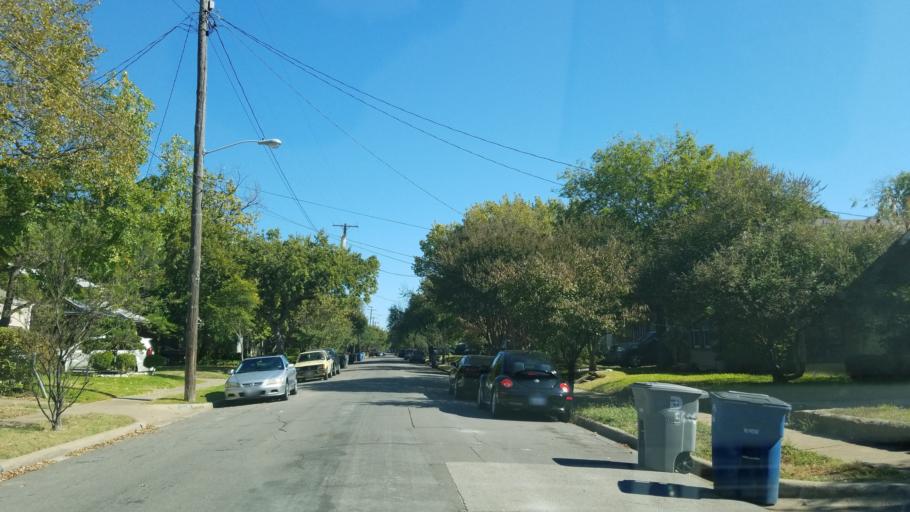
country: US
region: Texas
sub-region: Dallas County
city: Highland Park
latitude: 32.8044
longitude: -96.7598
